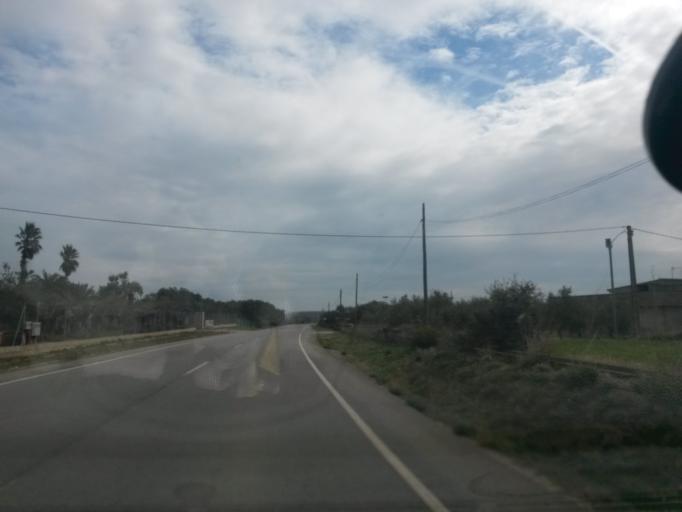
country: ES
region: Catalonia
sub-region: Provincia de Girona
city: Pont de Molins
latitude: 42.3136
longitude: 2.9535
